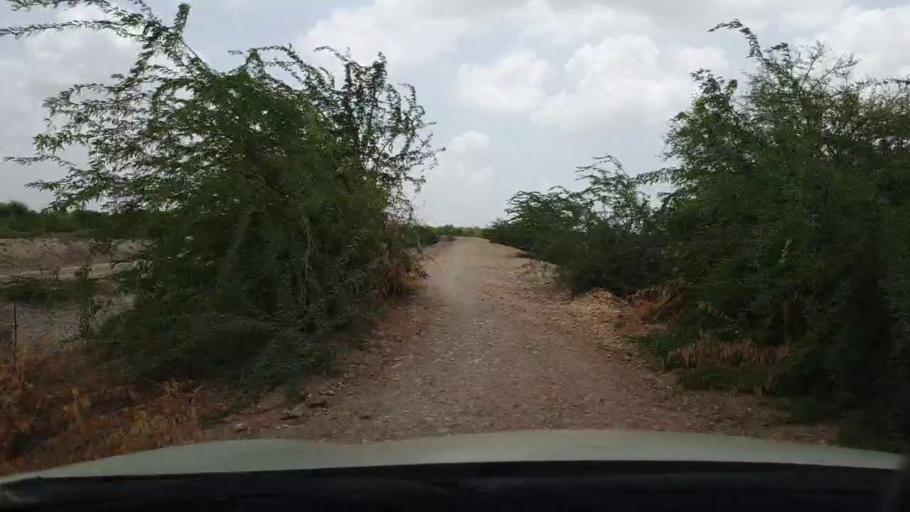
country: PK
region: Sindh
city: Kadhan
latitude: 24.3739
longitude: 68.9282
